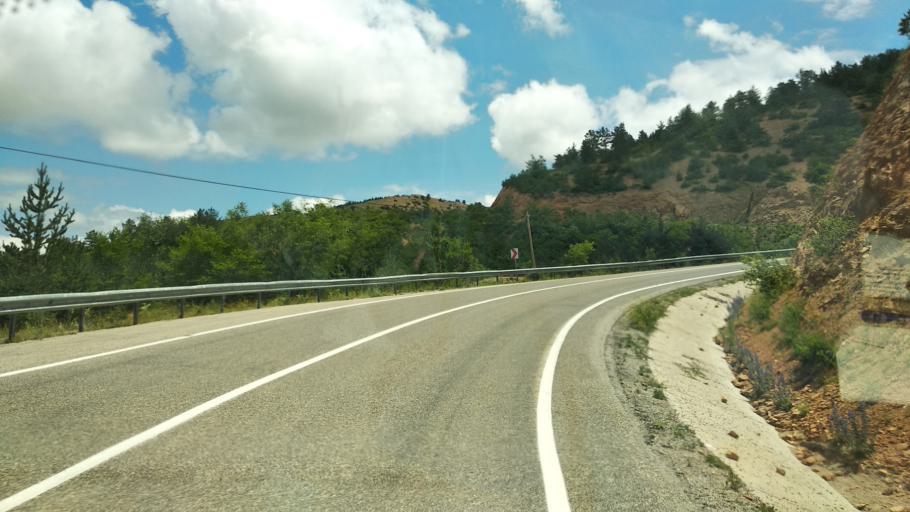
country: TR
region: Gumushane
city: Kose
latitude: 40.2987
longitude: 39.5622
